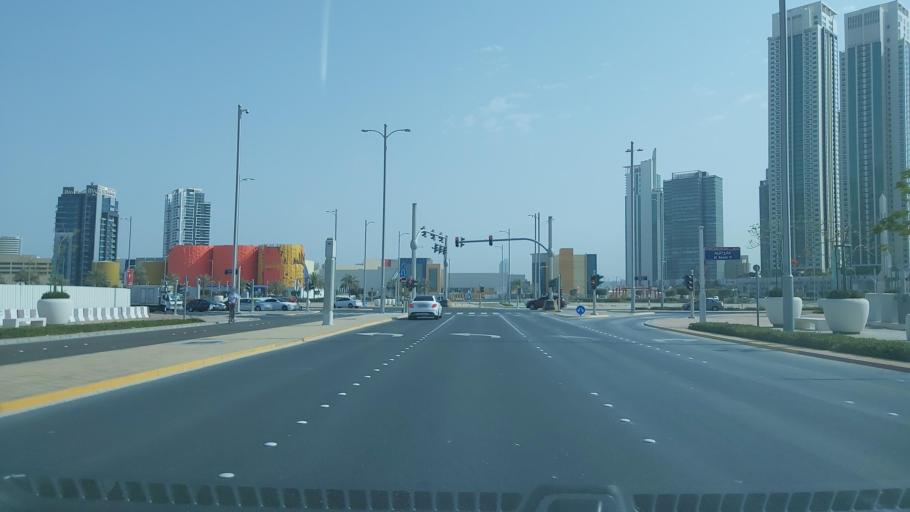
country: AE
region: Abu Dhabi
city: Abu Dhabi
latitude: 24.4951
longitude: 54.3981
